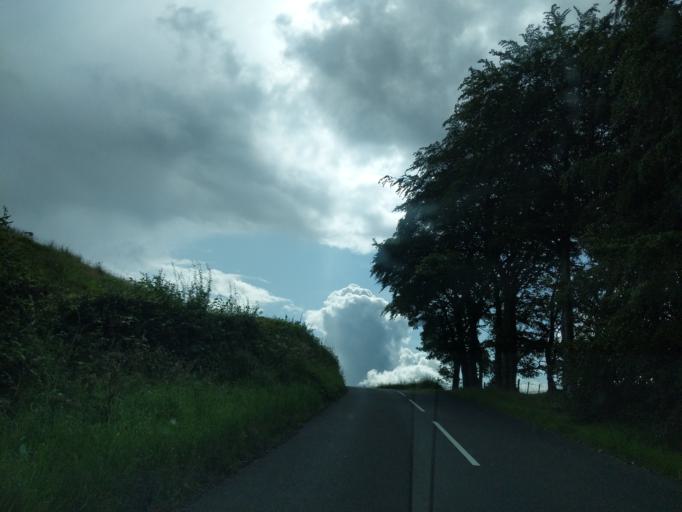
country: GB
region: Scotland
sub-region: East Renfrewshire
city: Neilston
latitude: 55.7498
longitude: -4.4617
